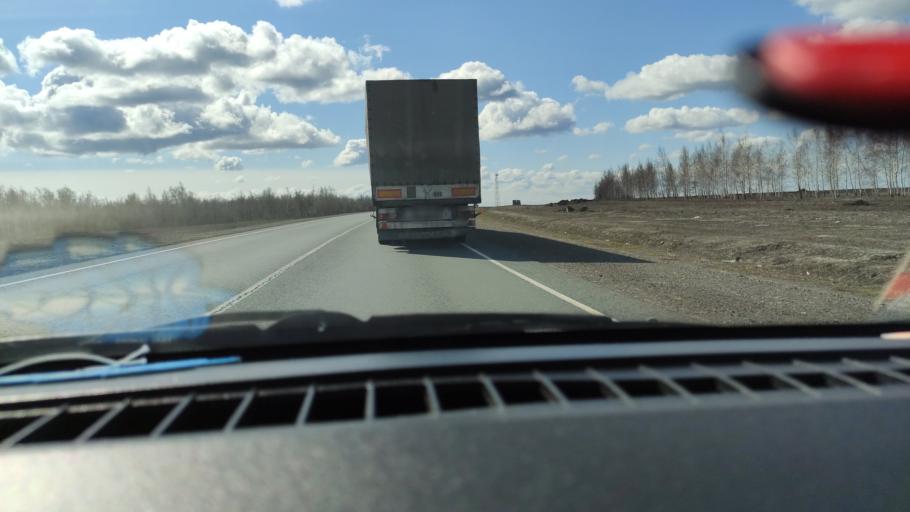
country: RU
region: Samara
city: Syzran'
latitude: 52.9315
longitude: 48.3069
